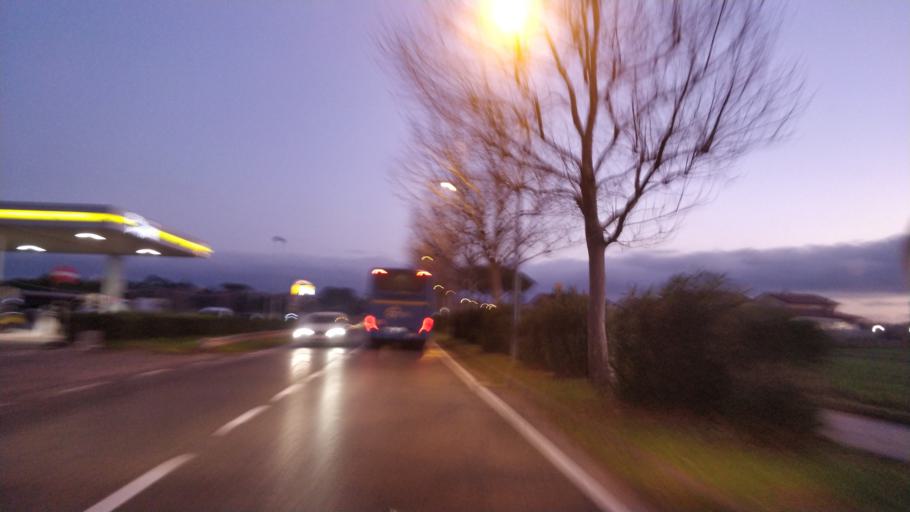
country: IT
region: Tuscany
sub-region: Provincia di Livorno
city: S.P. in Palazzi
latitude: 43.3200
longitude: 10.5119
